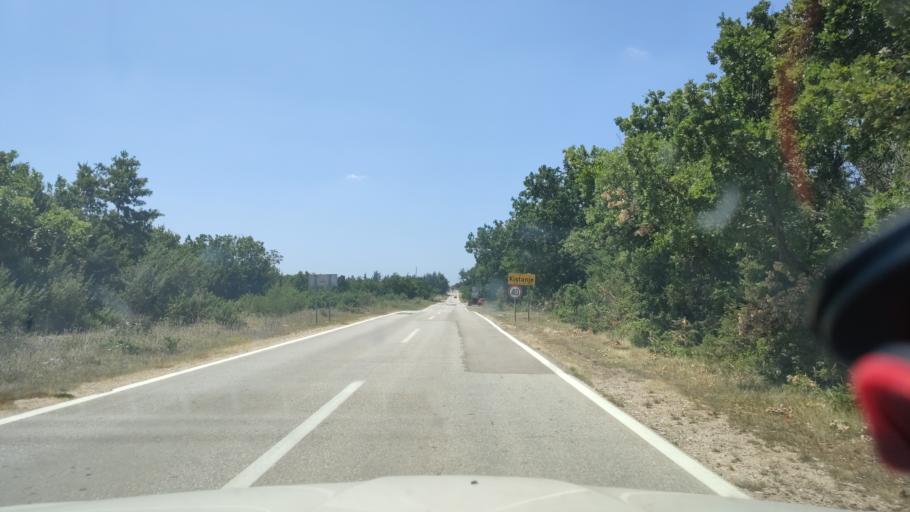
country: HR
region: Sibensko-Kniniska
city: Kistanje
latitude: 43.9912
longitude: 15.9785
